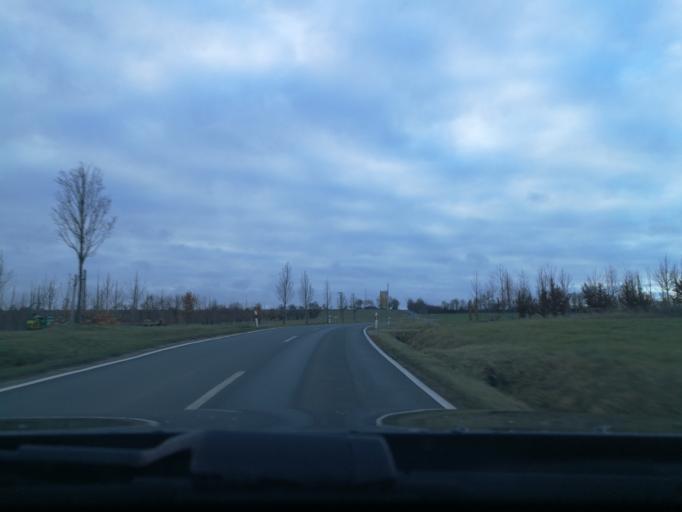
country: DE
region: Bavaria
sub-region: Regierungsbezirk Mittelfranken
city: Marloffstein
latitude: 49.6268
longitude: 11.0651
